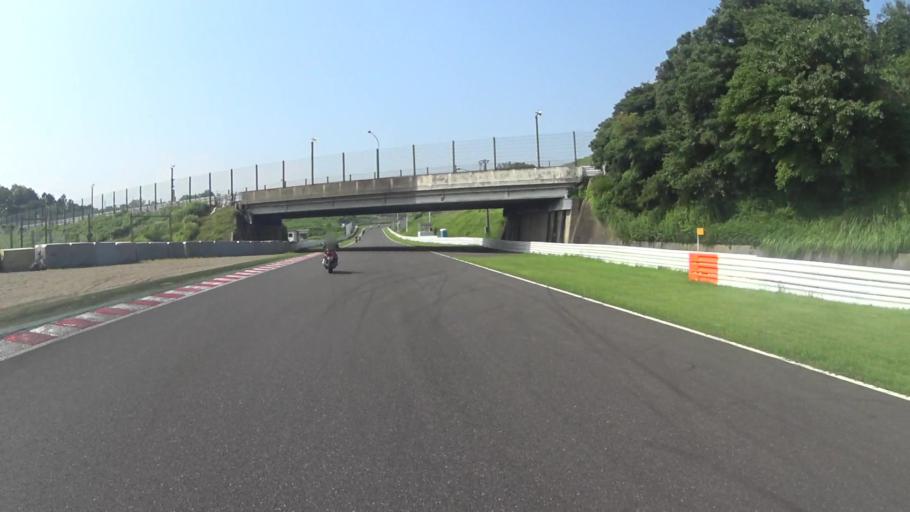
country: JP
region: Mie
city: Kawage
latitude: 34.8443
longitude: 136.5335
